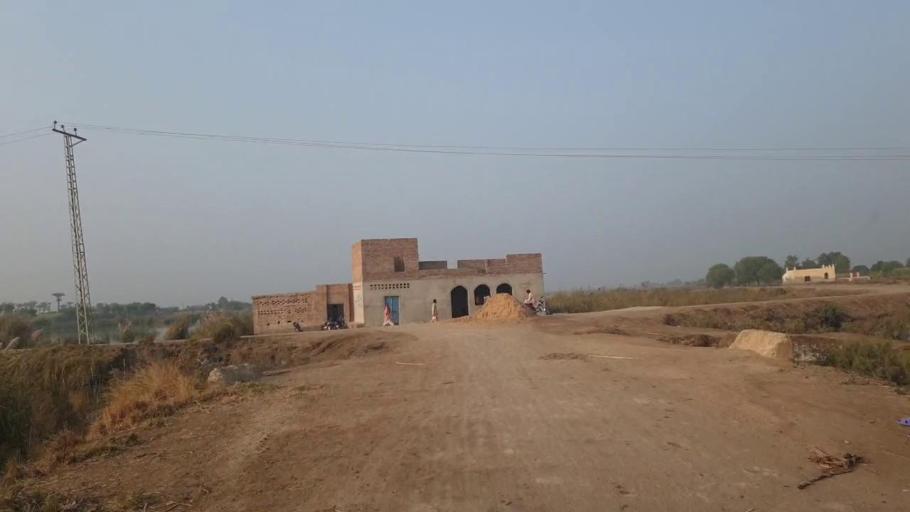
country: PK
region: Sindh
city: Shahdadpur
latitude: 25.8752
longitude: 68.6065
